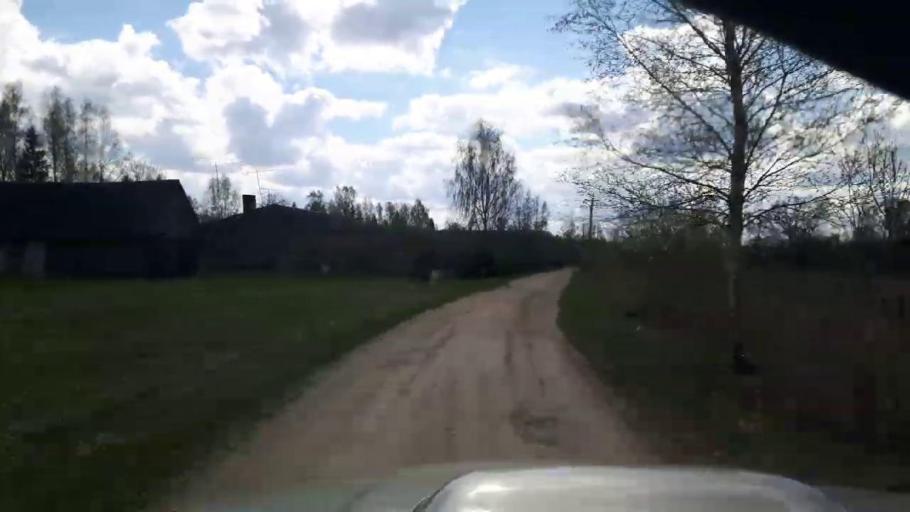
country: EE
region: Paernumaa
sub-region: Tootsi vald
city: Tootsi
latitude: 58.5010
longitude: 24.9301
